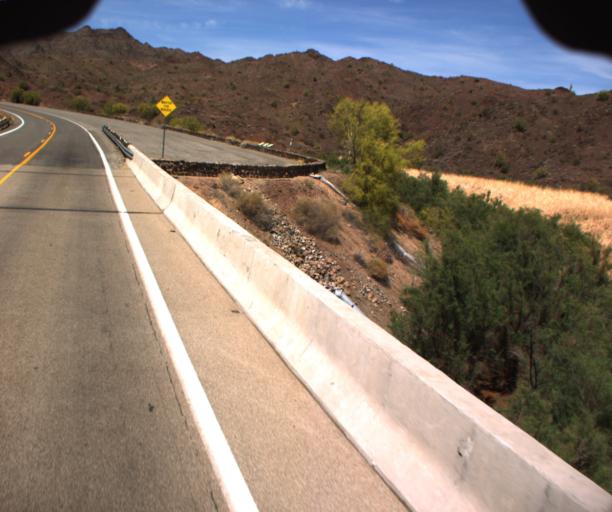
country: US
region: Arizona
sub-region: La Paz County
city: Cienega Springs
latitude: 34.3008
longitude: -114.0936
